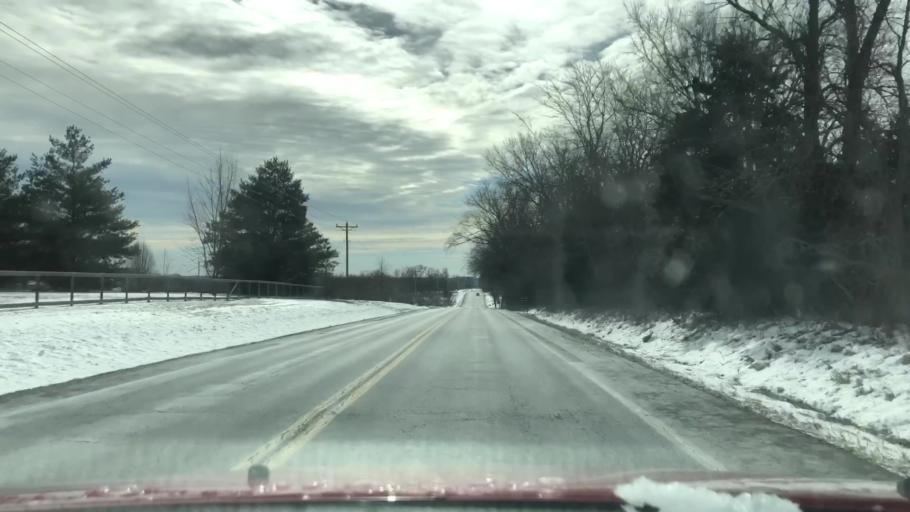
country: US
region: Missouri
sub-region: Jackson County
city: Lone Jack
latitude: 38.8823
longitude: -94.1350
